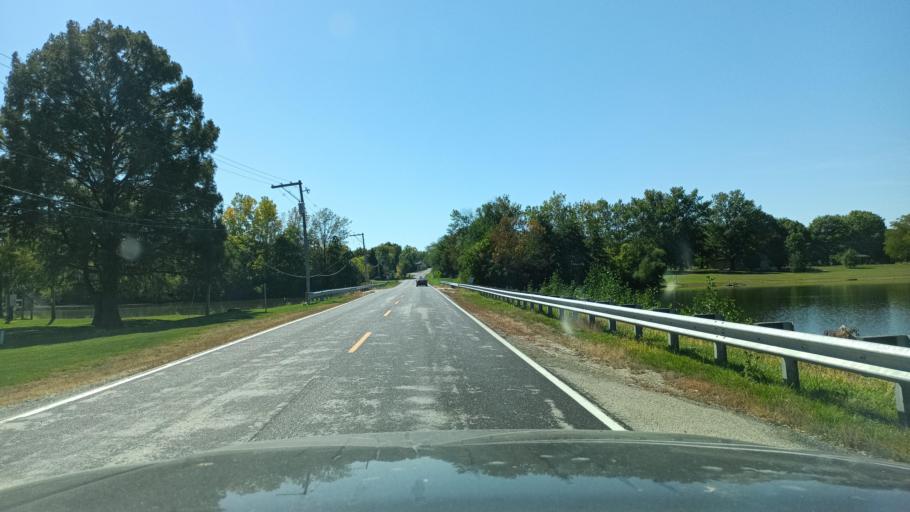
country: US
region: Illinois
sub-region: Champaign County
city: Lake of the Woods
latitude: 40.1998
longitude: -88.3755
